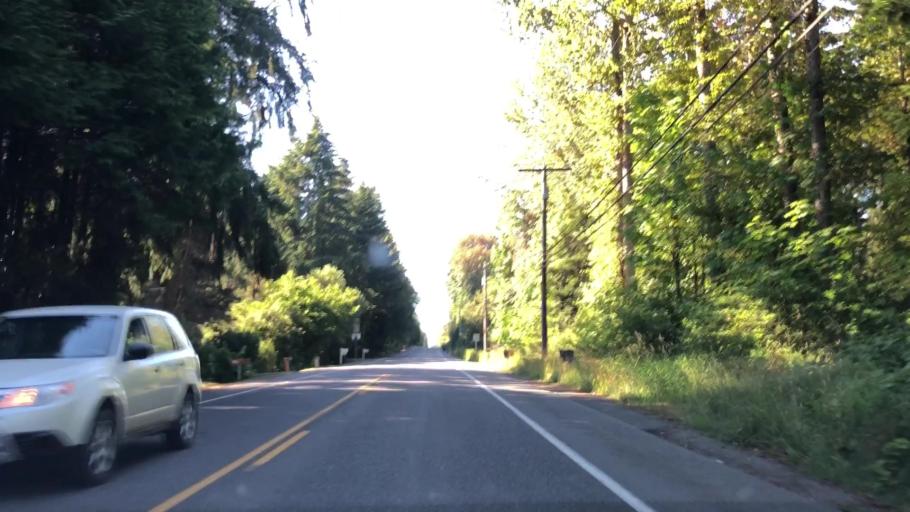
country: US
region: Washington
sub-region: Kitsap County
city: Kingston
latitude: 47.7913
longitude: -122.5054
